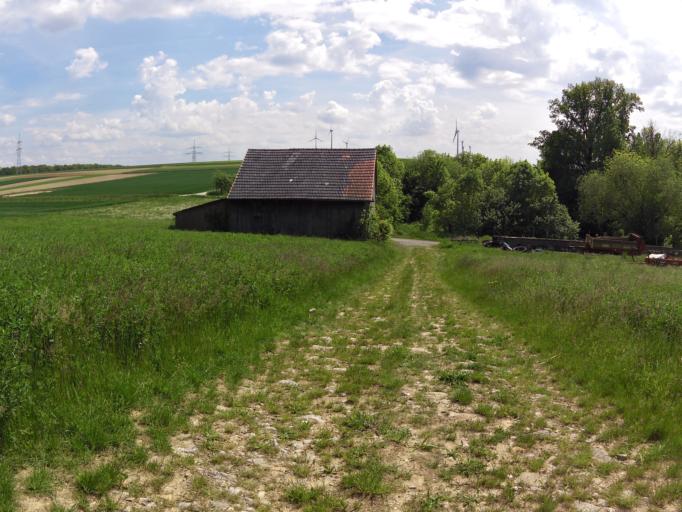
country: DE
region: Bavaria
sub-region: Regierungsbezirk Unterfranken
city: Theilheim
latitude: 49.7349
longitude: 10.0391
